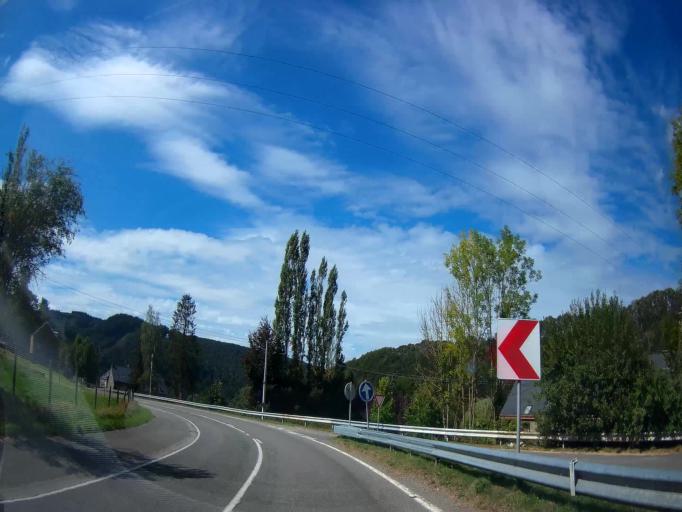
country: BE
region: Wallonia
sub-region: Province du Luxembourg
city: Rendeux
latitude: 50.2081
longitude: 5.5374
